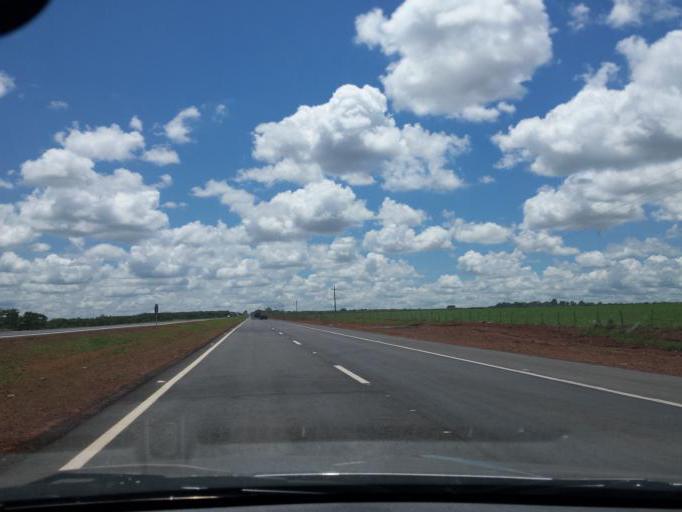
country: BR
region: Goias
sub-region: Cristalina
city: Cristalina
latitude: -16.7083
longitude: -47.6826
